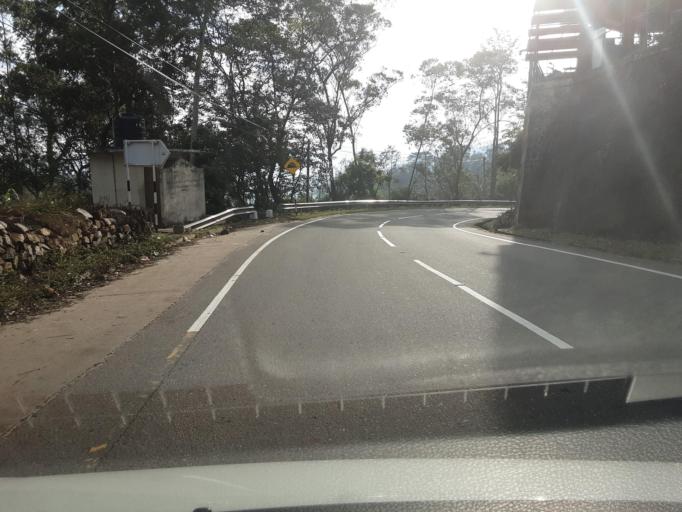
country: LK
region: Uva
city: Badulla
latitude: 6.9383
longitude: 80.9942
